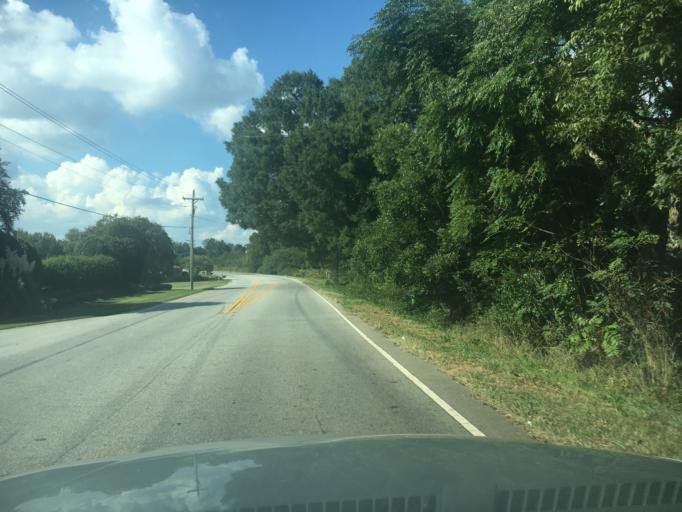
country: US
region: South Carolina
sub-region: Greenville County
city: Simpsonville
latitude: 34.6930
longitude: -82.2529
